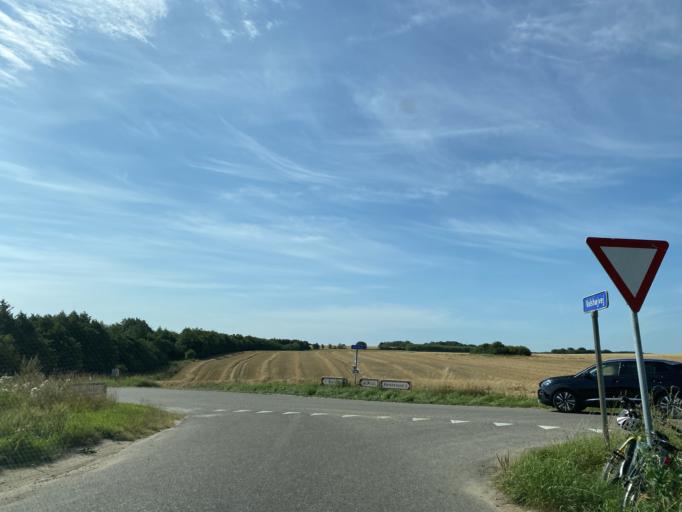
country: DK
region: Central Jutland
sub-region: Viborg Kommune
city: Bjerringbro
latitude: 56.3342
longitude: 9.7300
